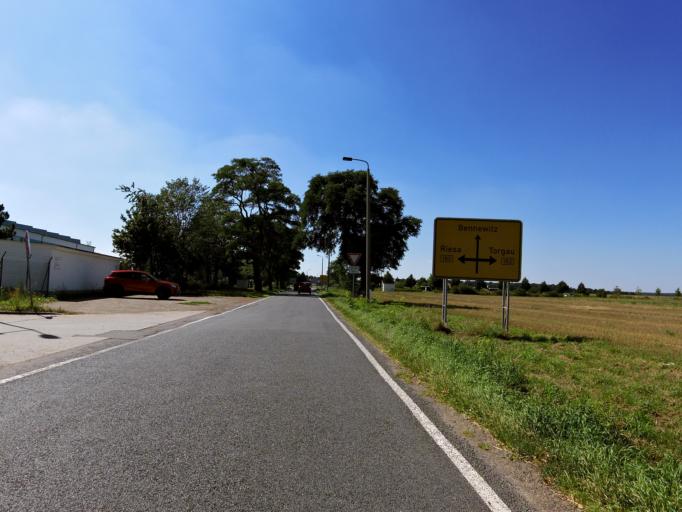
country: DE
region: Saxony
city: Beilrode
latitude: 51.5160
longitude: 13.0403
